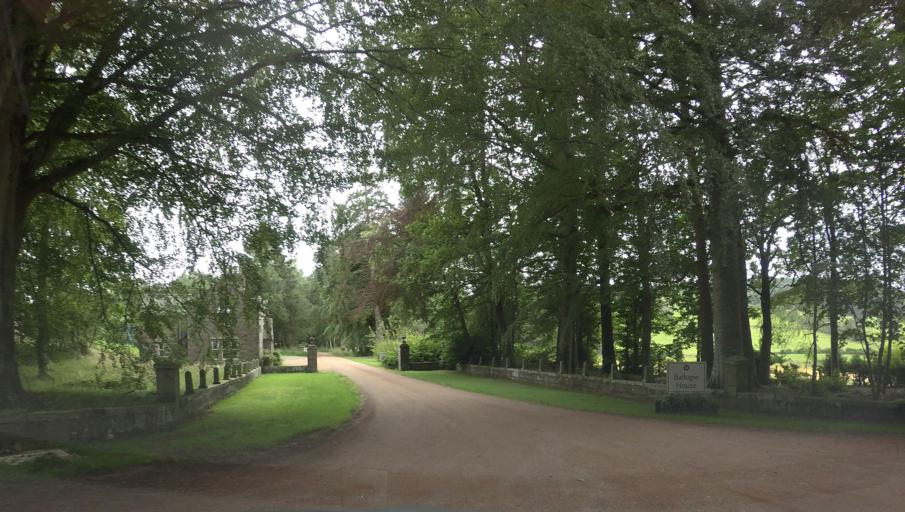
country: GB
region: Scotland
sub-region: Aberdeenshire
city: Aboyne
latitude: 57.0585
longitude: -2.7060
